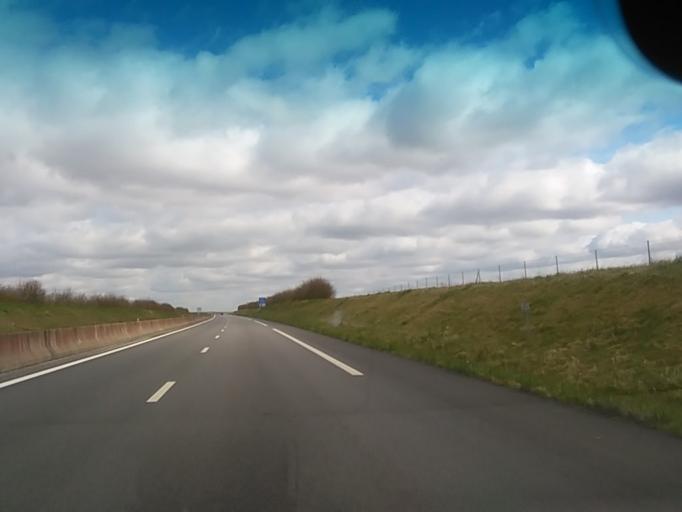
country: FR
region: Haute-Normandie
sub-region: Departement de l'Eure
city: Menneval
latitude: 49.1465
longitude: 0.6007
